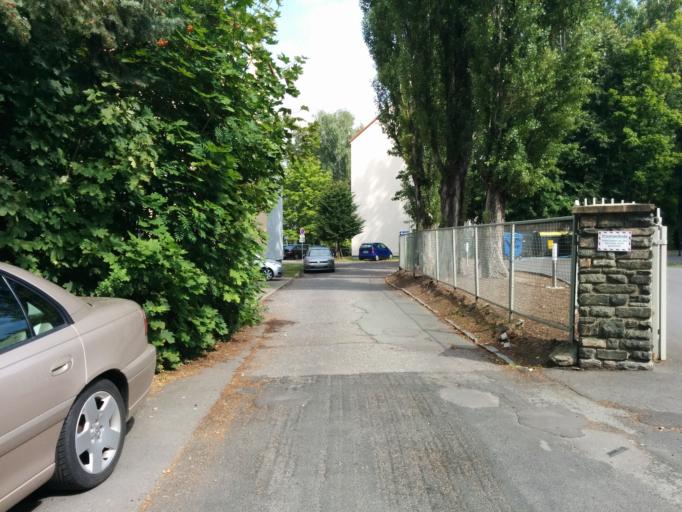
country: DE
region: Saxony
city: Chemnitz
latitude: 50.8070
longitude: 12.9159
